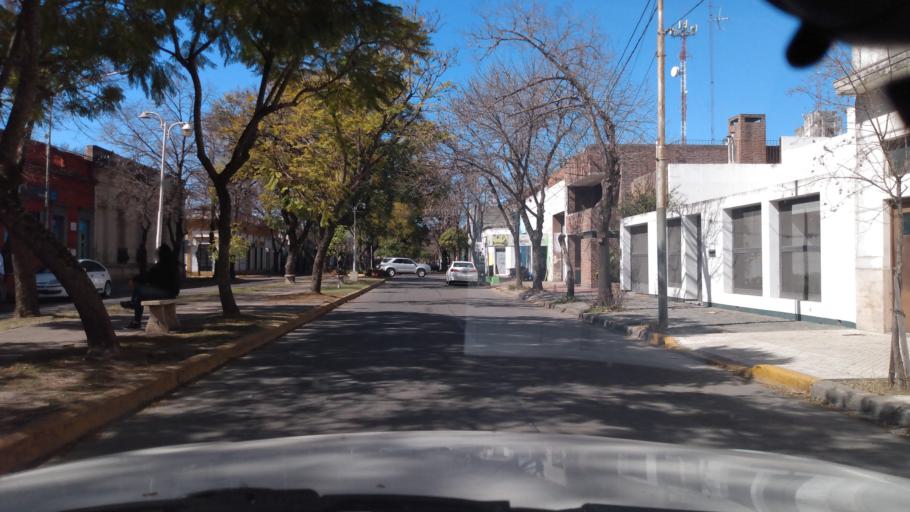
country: AR
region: Buenos Aires
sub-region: Partido de Mercedes
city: Mercedes
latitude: -34.6489
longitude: -59.4312
